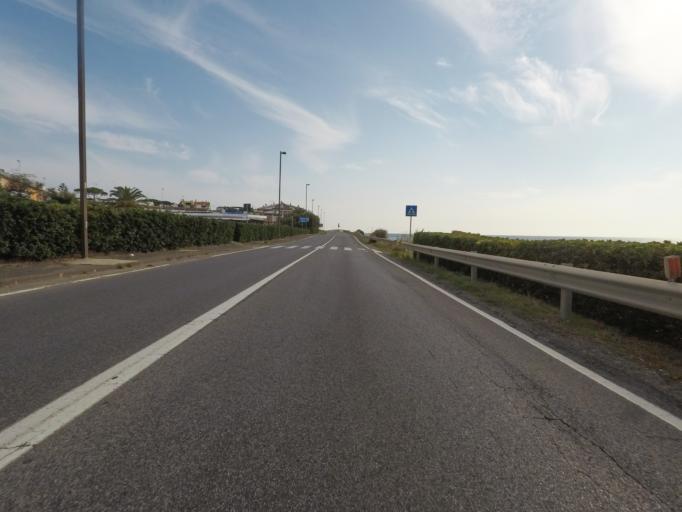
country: IT
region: Latium
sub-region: Citta metropolitana di Roma Capitale
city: Santa Marinella
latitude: 42.0439
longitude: 11.8271
